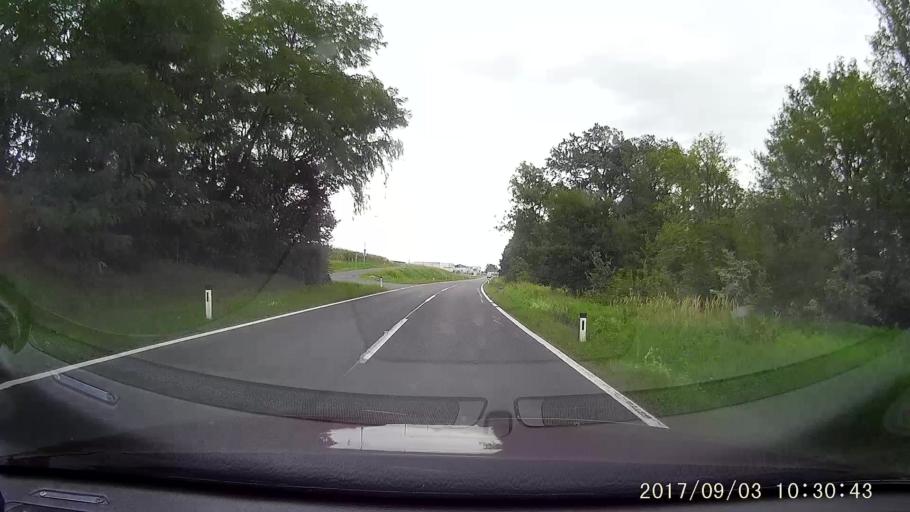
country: AT
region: Styria
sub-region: Politischer Bezirk Hartberg-Fuerstenfeld
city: Ilz
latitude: 47.0833
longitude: 15.9496
